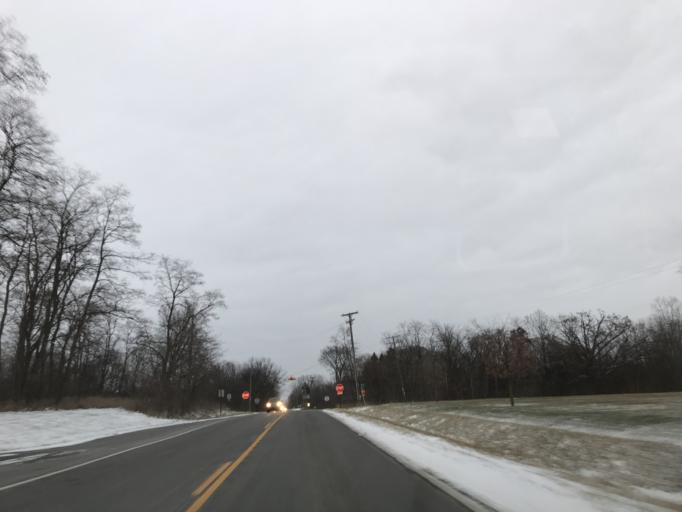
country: US
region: Michigan
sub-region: Oakland County
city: South Lyon
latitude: 42.3621
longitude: -83.6639
